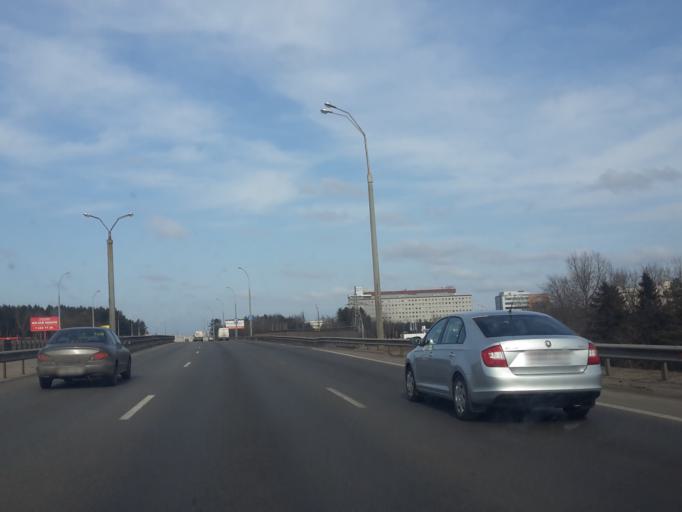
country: BY
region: Minsk
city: Vyaliki Trastsyanets
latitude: 53.9210
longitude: 27.6815
